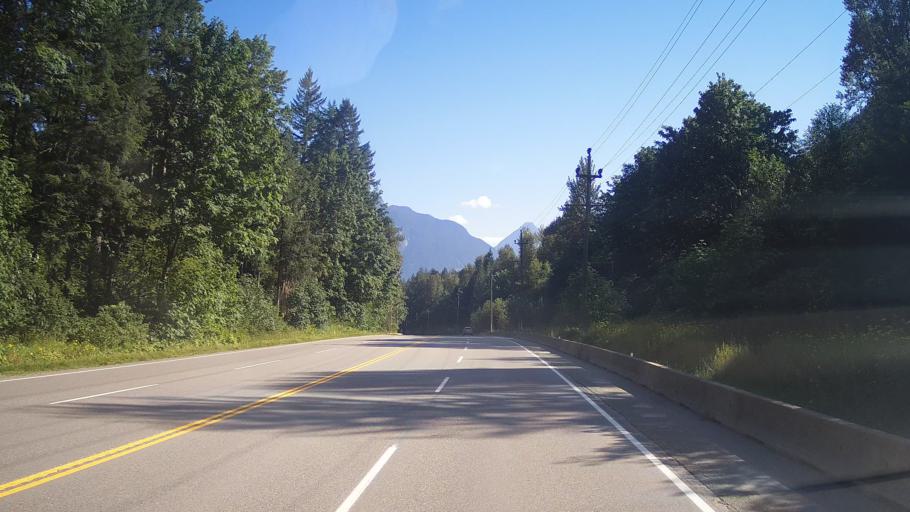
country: CA
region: British Columbia
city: Hope
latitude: 49.4504
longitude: -121.4375
